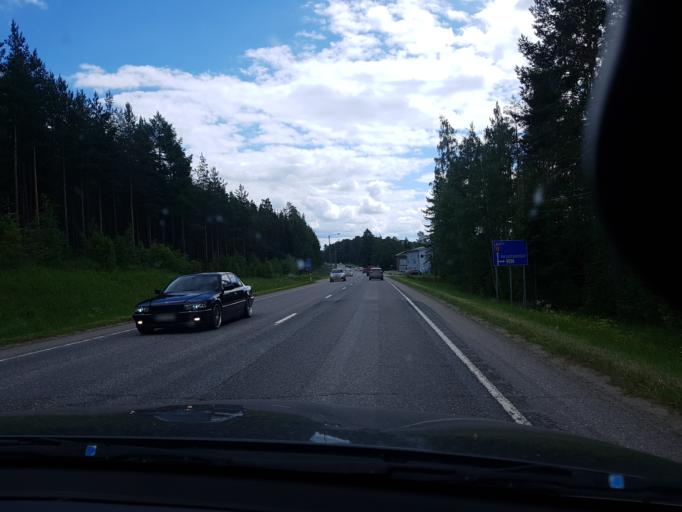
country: FI
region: Pirkanmaa
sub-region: Tampere
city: Paelkaene
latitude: 61.3032
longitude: 24.3002
